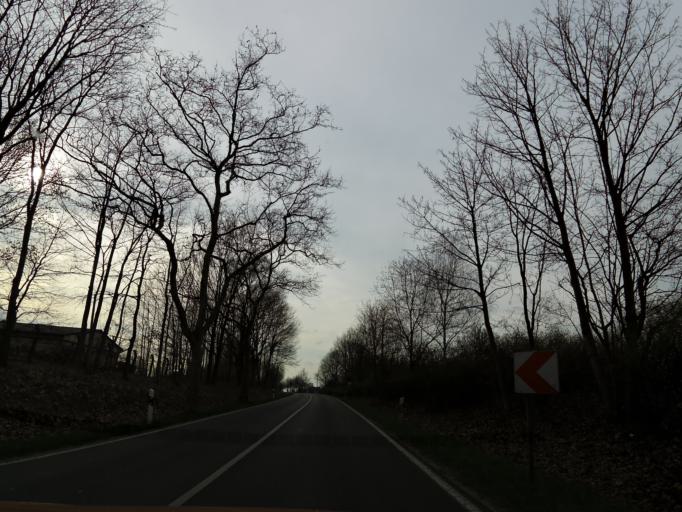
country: DE
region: Brandenburg
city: Bestensee
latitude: 52.2435
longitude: 13.6057
